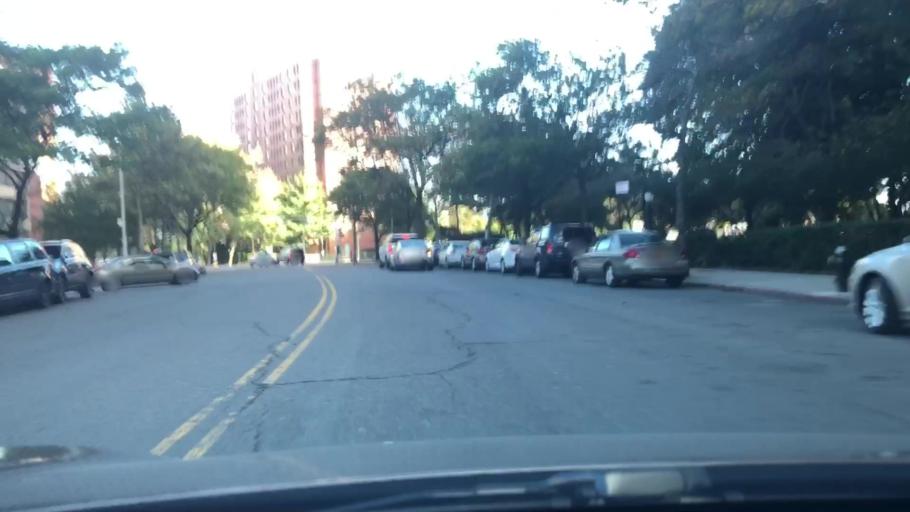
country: US
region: New York
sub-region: Bronx
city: Eastchester
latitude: 40.8774
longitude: -73.8280
